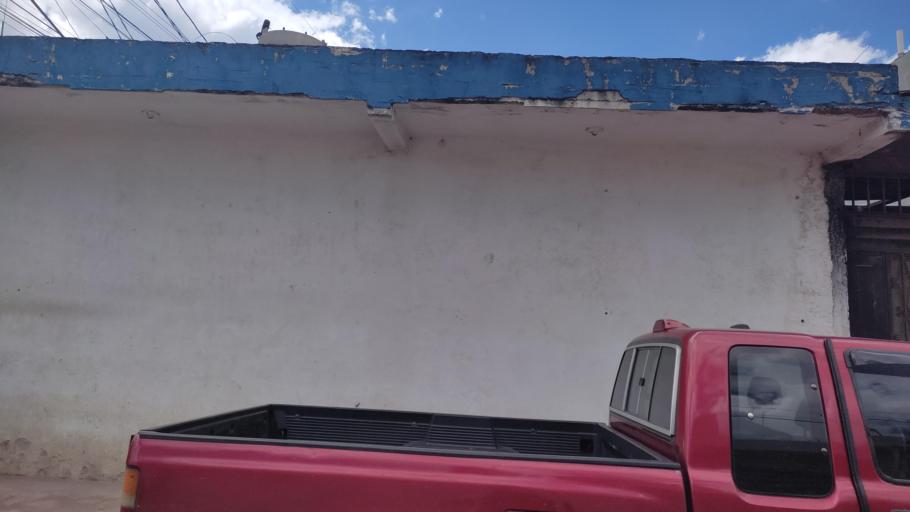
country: GT
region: Quetzaltenango
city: Olintepeque
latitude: 14.8614
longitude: -91.5223
